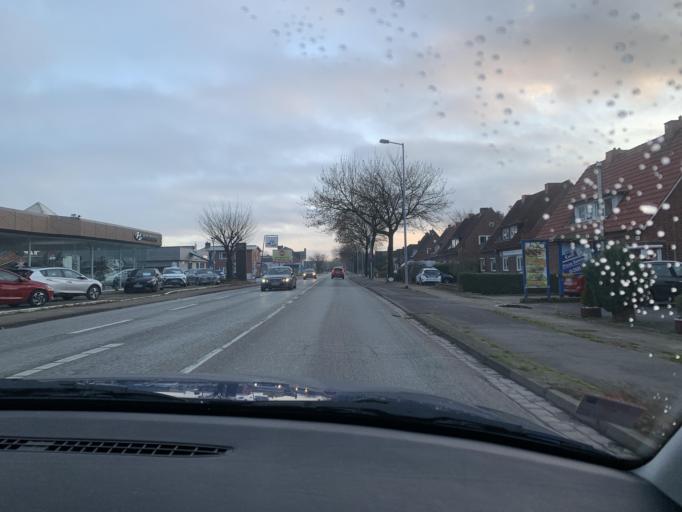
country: DE
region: Schleswig-Holstein
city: Heide
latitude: 54.1859
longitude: 9.0901
